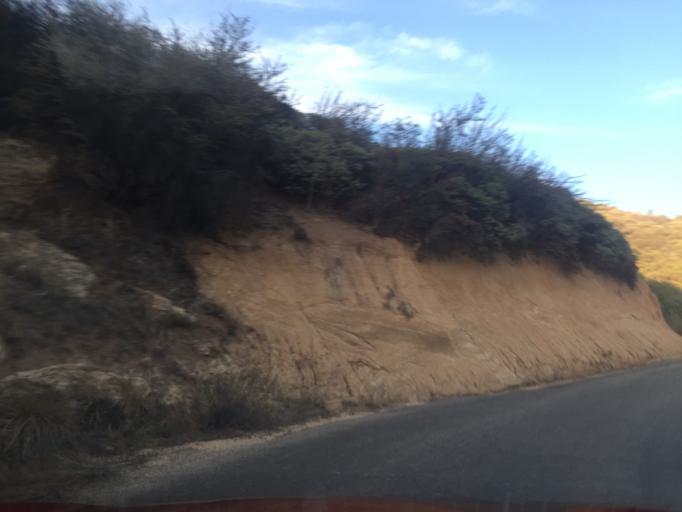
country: US
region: California
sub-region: Tulare County
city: Three Rivers
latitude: 36.4366
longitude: -118.7347
